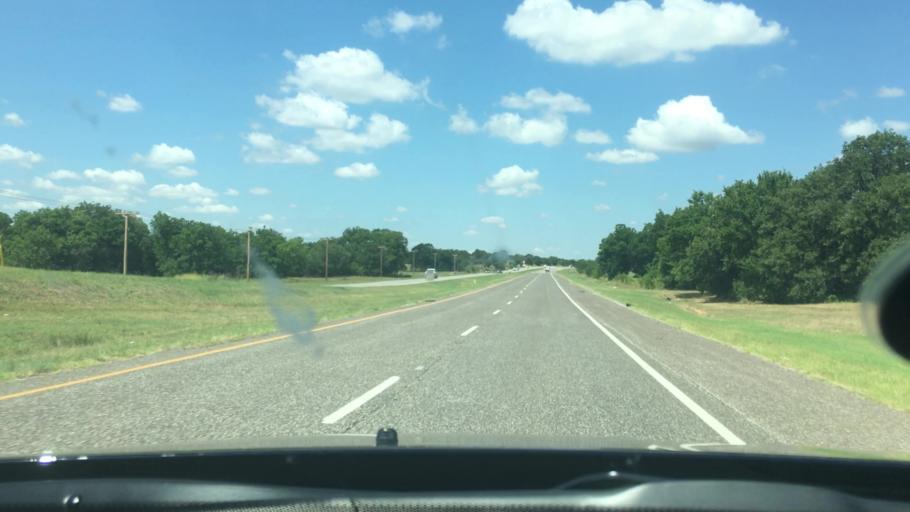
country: US
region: Oklahoma
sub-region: Carter County
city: Wilson
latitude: 34.1730
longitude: -97.3532
